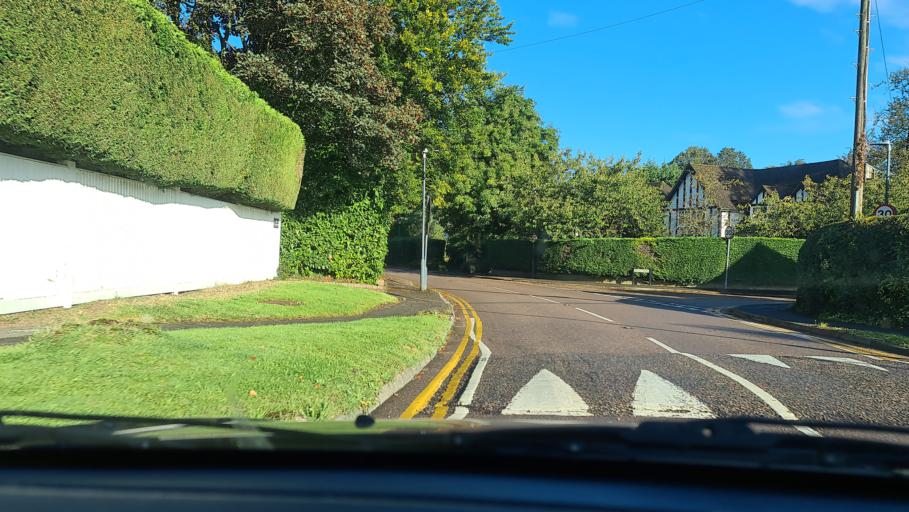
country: GB
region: England
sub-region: Buckinghamshire
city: Chalfont St Giles
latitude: 51.6480
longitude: -0.5287
